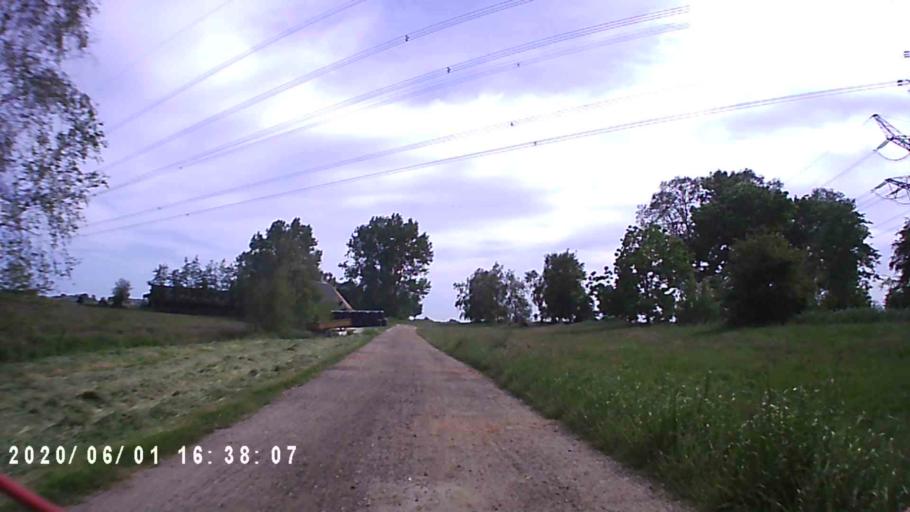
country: NL
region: Friesland
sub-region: Gemeente Leeuwarden
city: Camminghaburen
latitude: 53.1888
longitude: 5.8772
